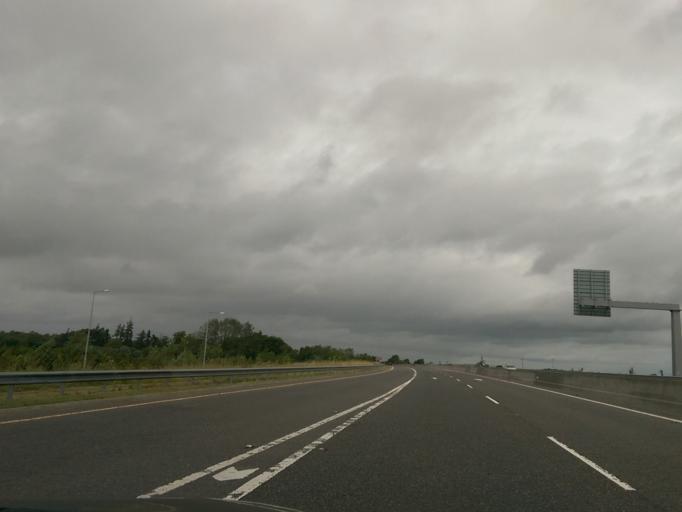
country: IE
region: Munster
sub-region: An Clar
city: Newmarket on Fergus
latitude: 52.7925
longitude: -8.9209
